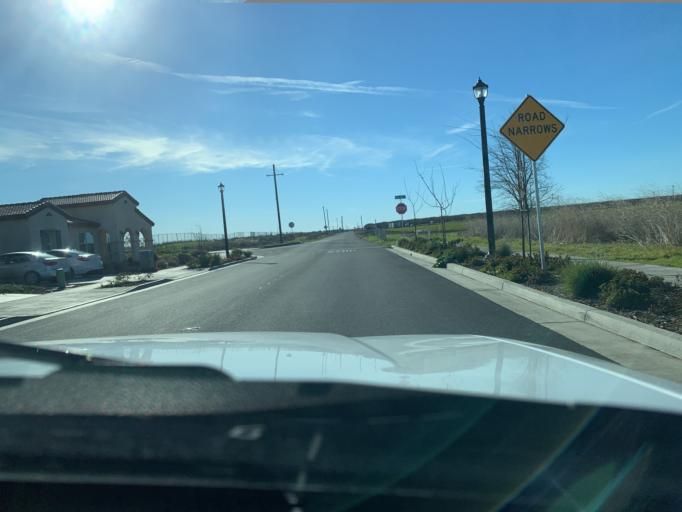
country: US
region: California
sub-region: Yolo County
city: Woodland
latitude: 38.6453
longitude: -121.7473
